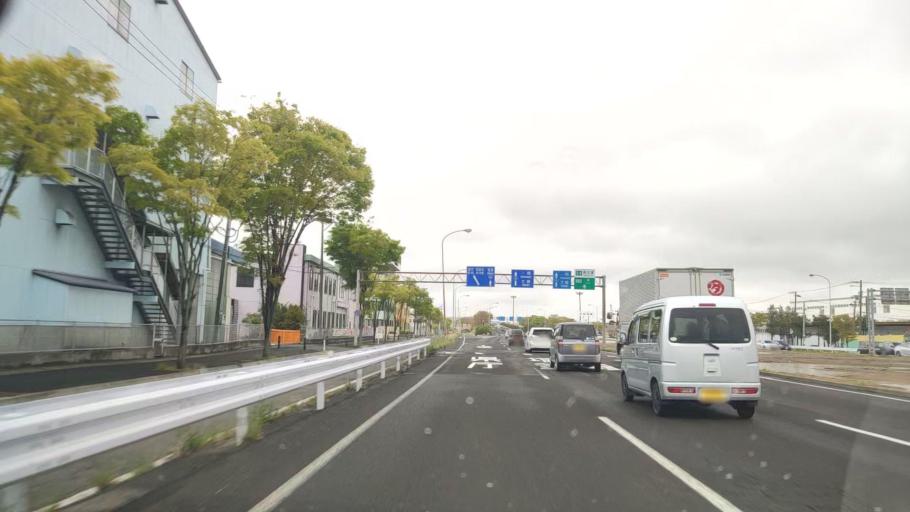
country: JP
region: Miyagi
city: Sendai-shi
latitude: 38.2629
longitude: 140.9378
